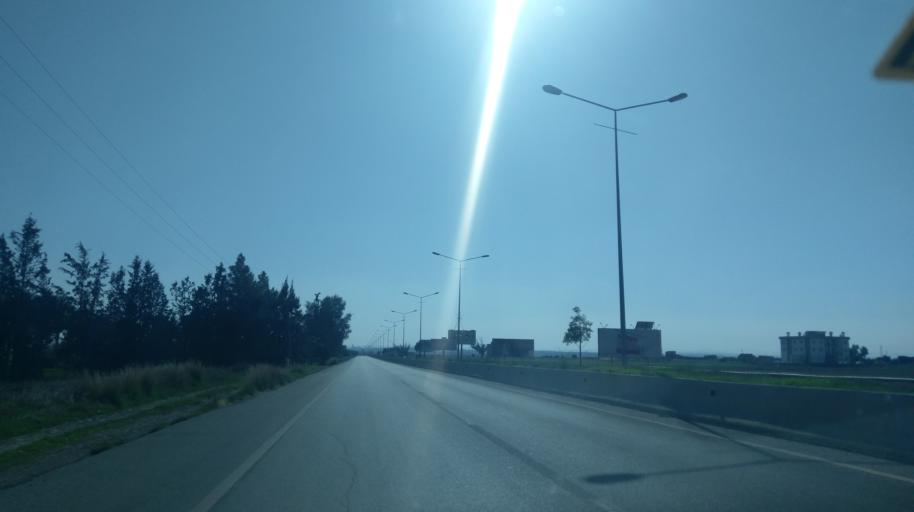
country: CY
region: Lefkosia
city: Geri
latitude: 35.2060
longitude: 33.4992
